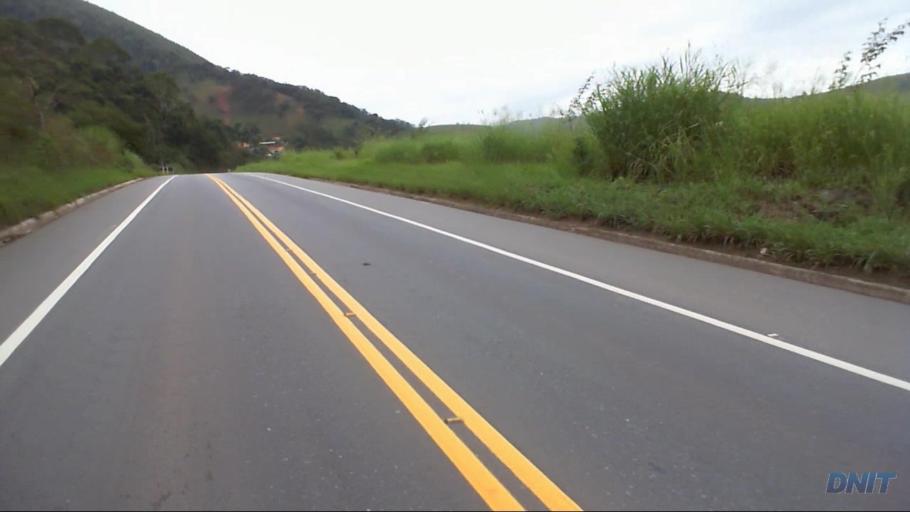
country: BR
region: Minas Gerais
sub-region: Nova Era
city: Nova Era
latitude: -19.7354
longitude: -43.0183
